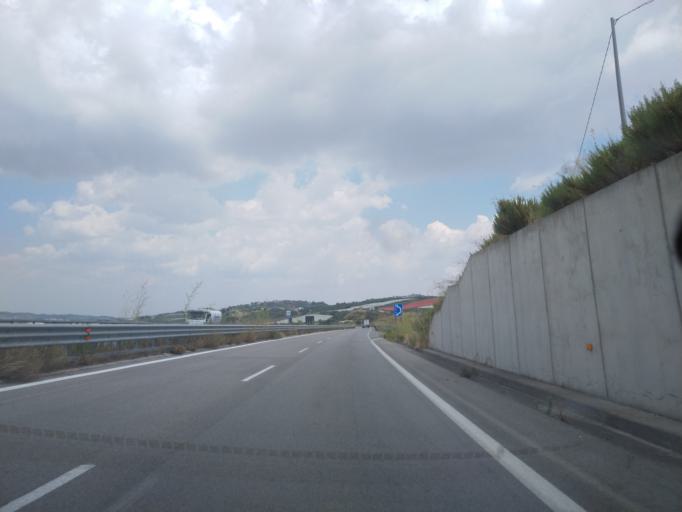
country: IT
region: Sicily
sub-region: Agrigento
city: Canicatti
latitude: 37.3834
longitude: 13.8170
